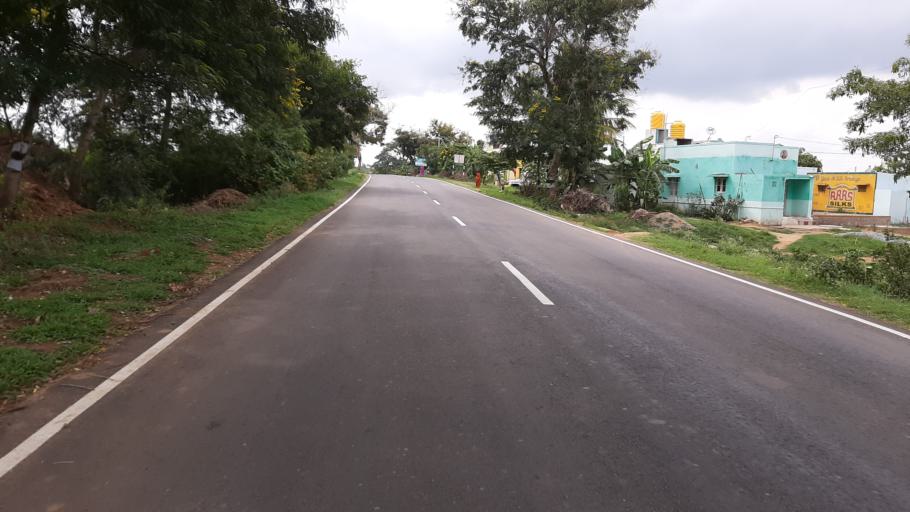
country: IN
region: Tamil Nadu
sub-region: Krishnagiri
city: Denkanikota
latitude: 12.5375
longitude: 77.7695
